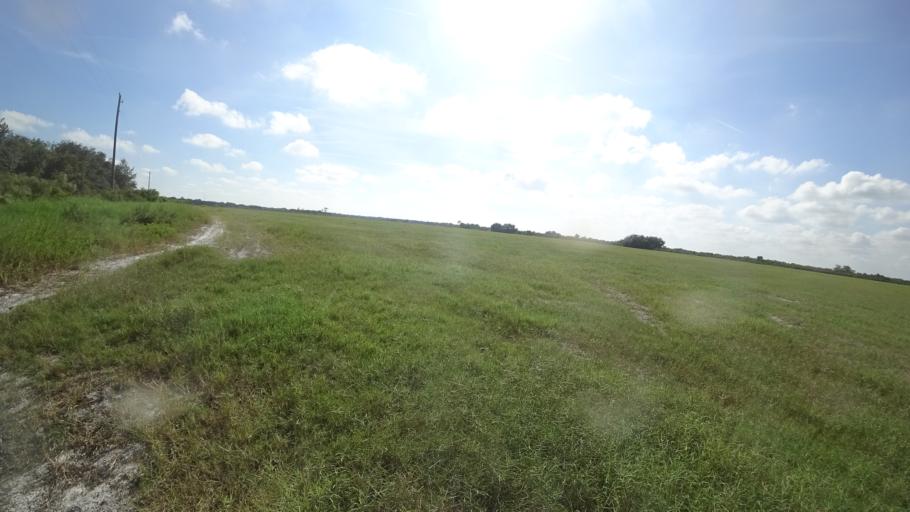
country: US
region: Florida
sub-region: Sarasota County
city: Lake Sarasota
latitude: 27.3729
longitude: -82.1676
